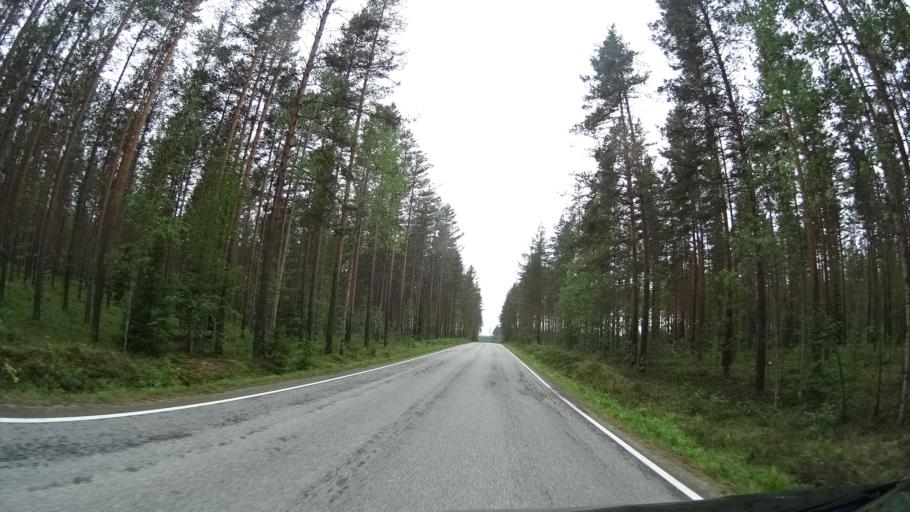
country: FI
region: Southern Savonia
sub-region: Savonlinna
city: Punkaharju
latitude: 61.7492
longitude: 29.4864
